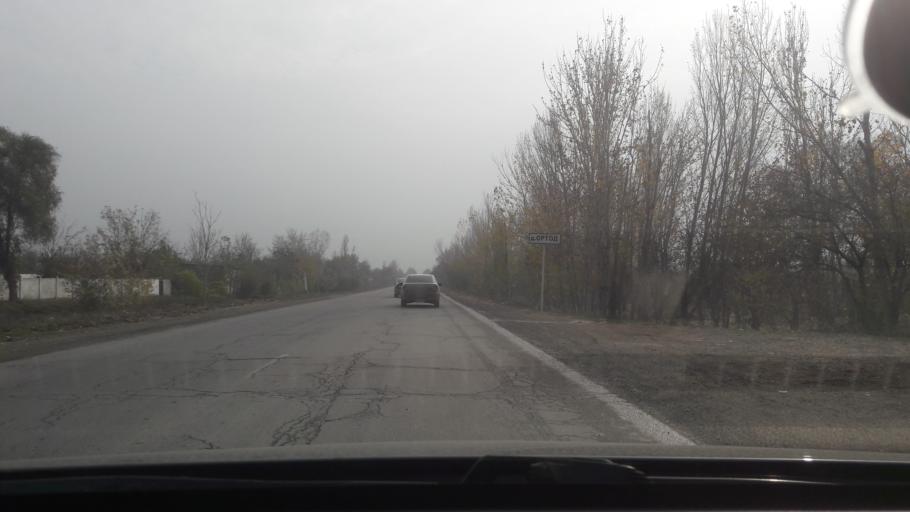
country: TJ
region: Khatlon
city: Qurghonteppa
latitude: 37.8746
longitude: 68.6983
